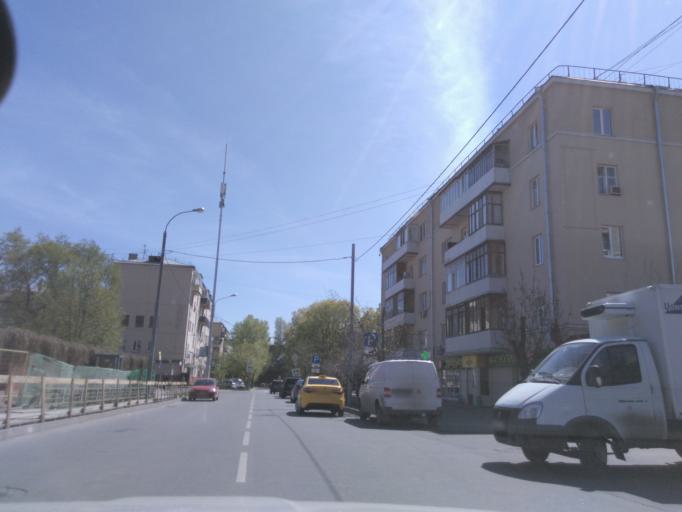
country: RU
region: Moscow
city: Luzhniki
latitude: 55.7231
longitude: 37.5655
